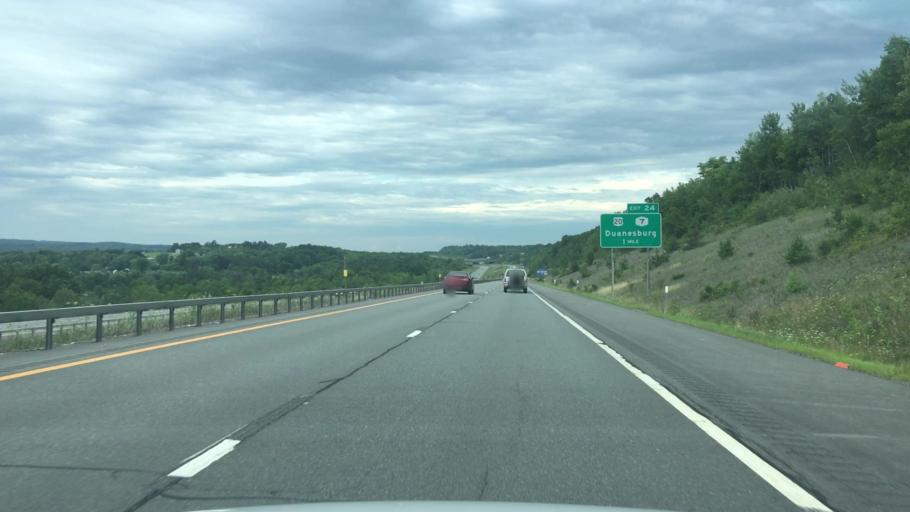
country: US
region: New York
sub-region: Albany County
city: Altamont
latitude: 42.7545
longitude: -74.1405
